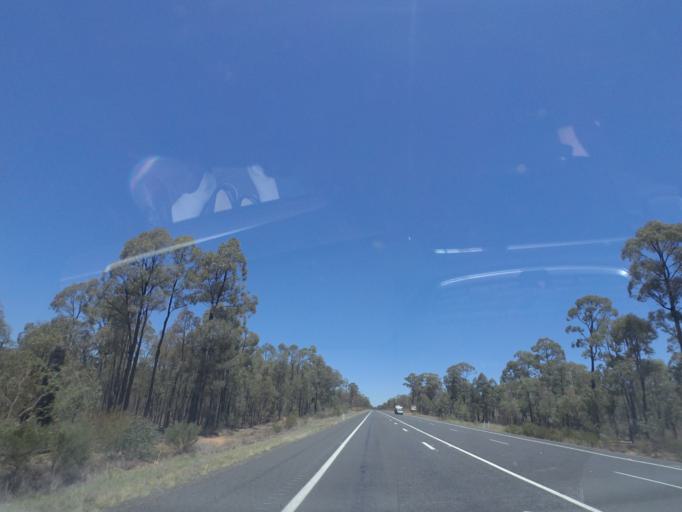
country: AU
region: New South Wales
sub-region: Warrumbungle Shire
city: Coonabarabran
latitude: -30.8695
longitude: 149.4508
